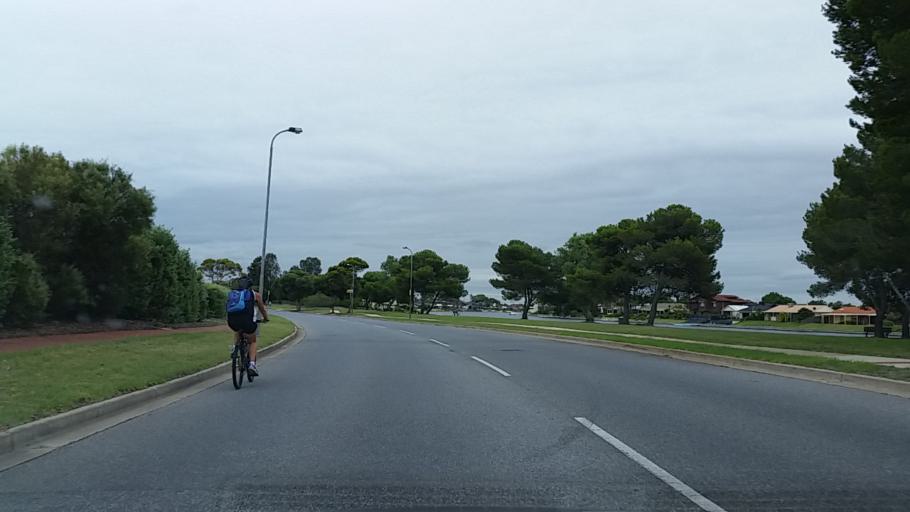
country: AU
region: South Australia
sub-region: Charles Sturt
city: West Lakes Shore
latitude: -34.8727
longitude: 138.4923
